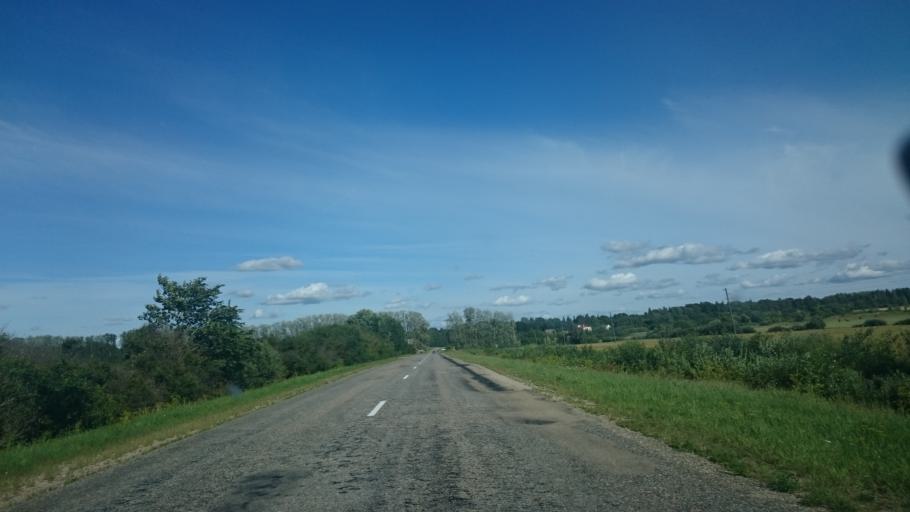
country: LV
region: Aizpute
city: Aizpute
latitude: 56.7316
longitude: 21.7163
